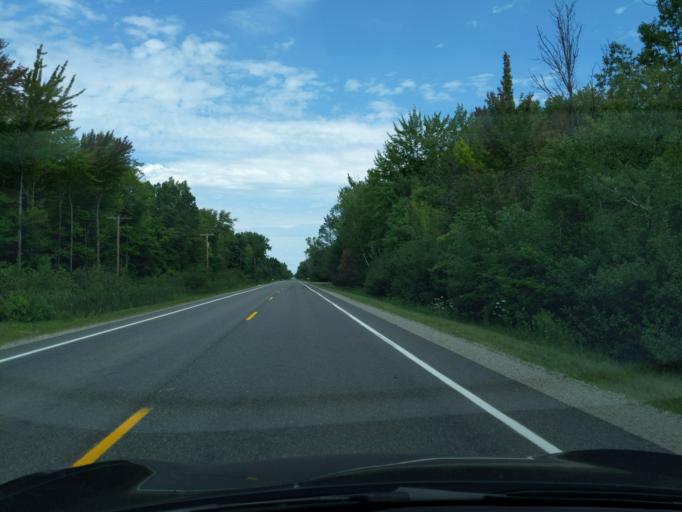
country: US
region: Michigan
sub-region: Midland County
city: Midland
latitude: 43.5343
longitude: -84.3698
